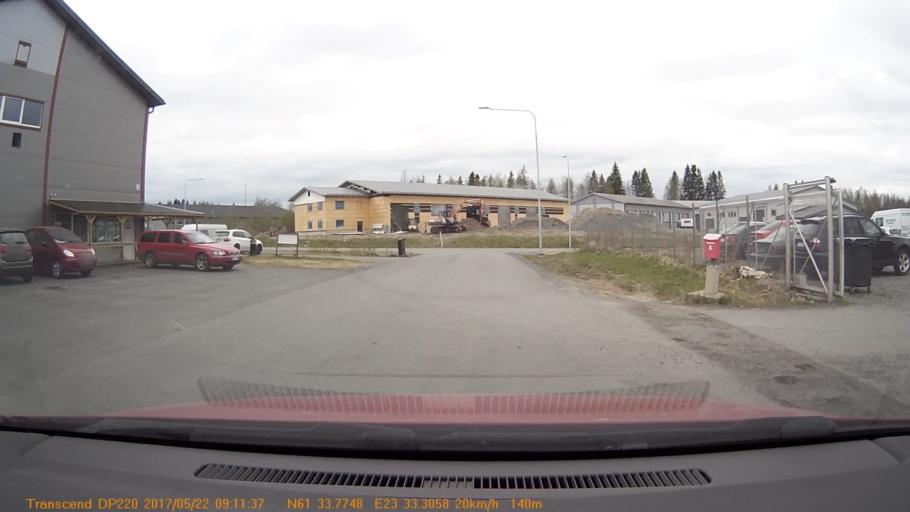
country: FI
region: Pirkanmaa
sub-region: Tampere
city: Yloejaervi
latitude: 61.5629
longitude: 23.5551
